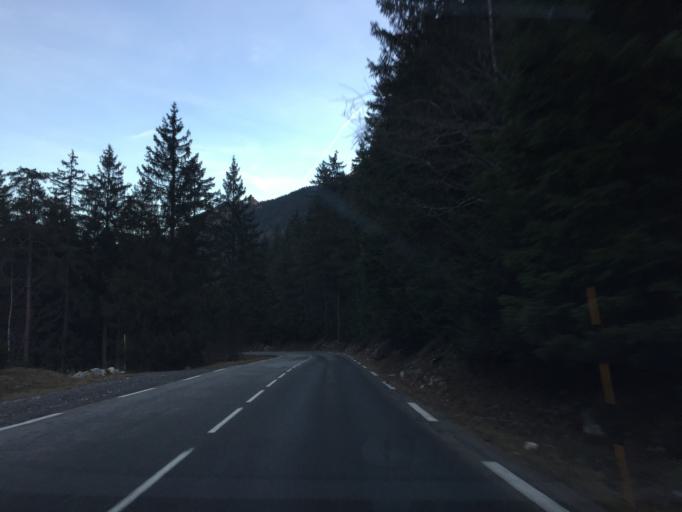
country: FR
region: Rhone-Alpes
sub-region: Departement de la Savoie
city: Bozel
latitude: 45.4089
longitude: 6.7088
